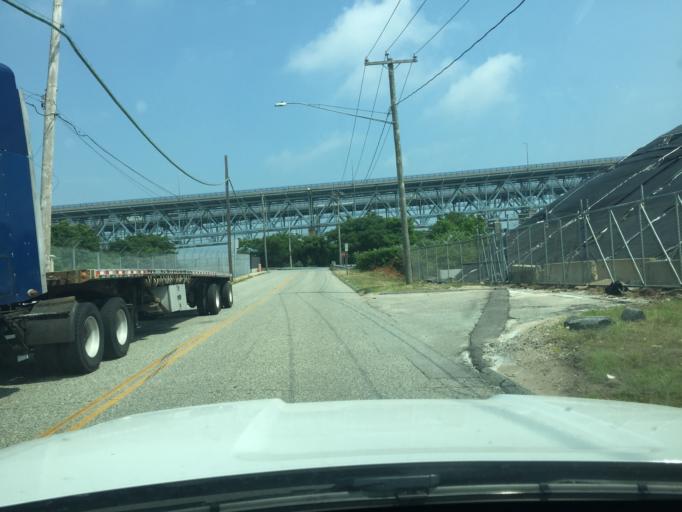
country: US
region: Connecticut
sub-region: New London County
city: New London
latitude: 41.3613
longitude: -72.0920
